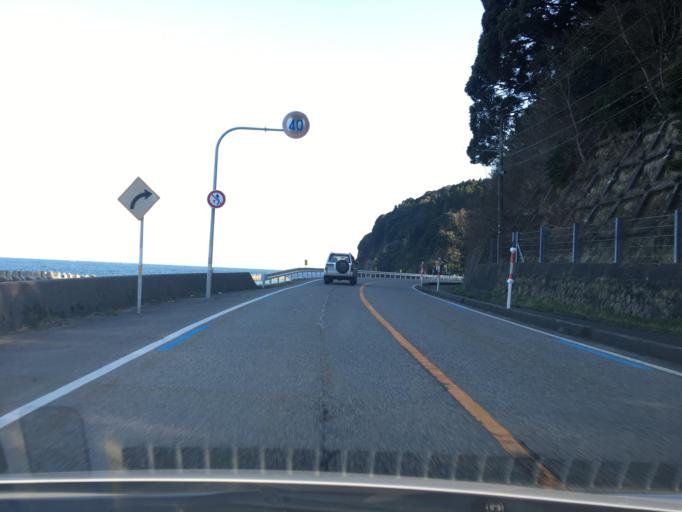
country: JP
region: Toyama
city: Himi
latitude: 36.9351
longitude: 137.0273
